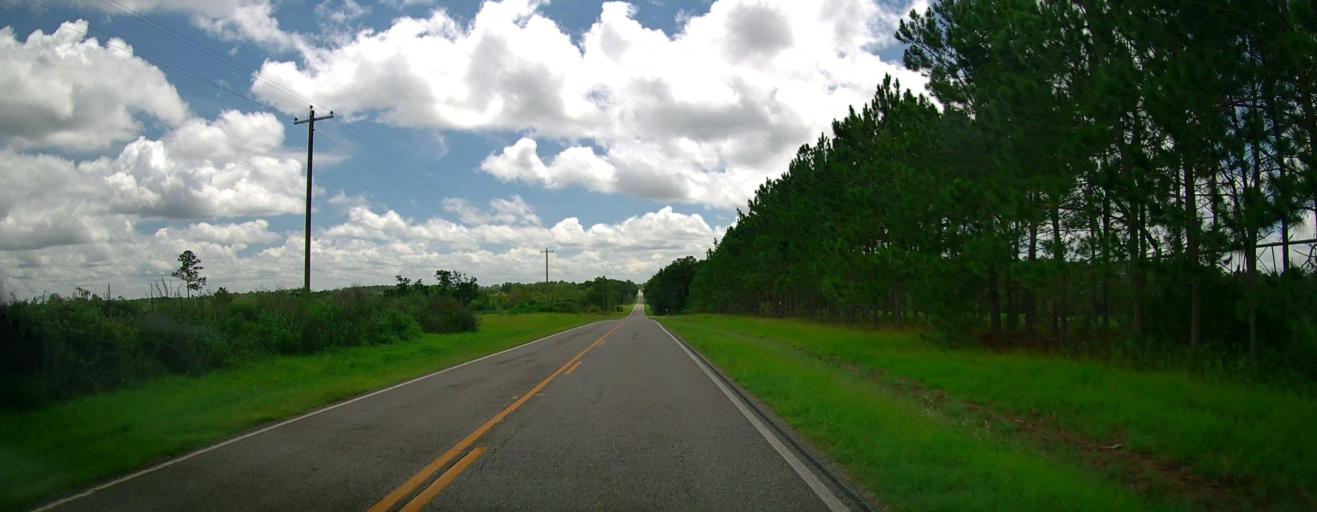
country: US
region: Georgia
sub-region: Wilcox County
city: Rochelle
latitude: 31.9168
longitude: -83.5532
